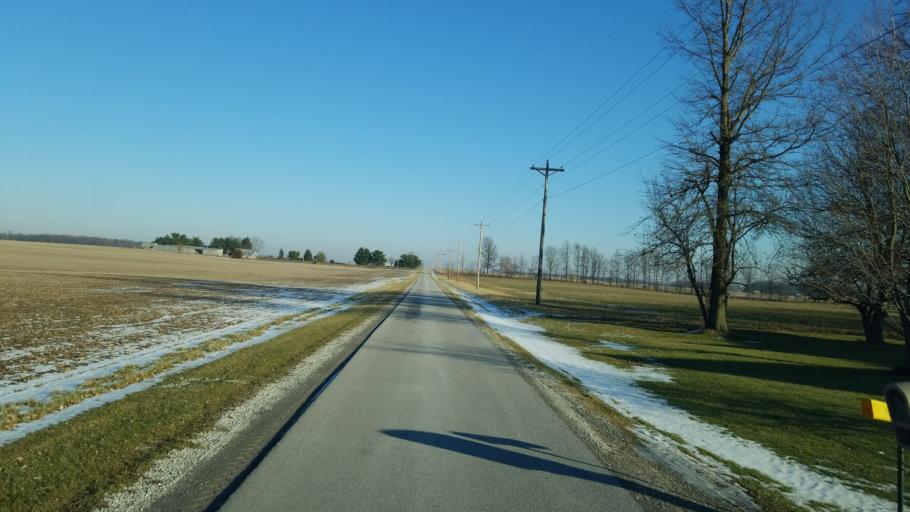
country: US
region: Ohio
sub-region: Crawford County
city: Bucyrus
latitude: 41.0083
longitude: -82.9919
